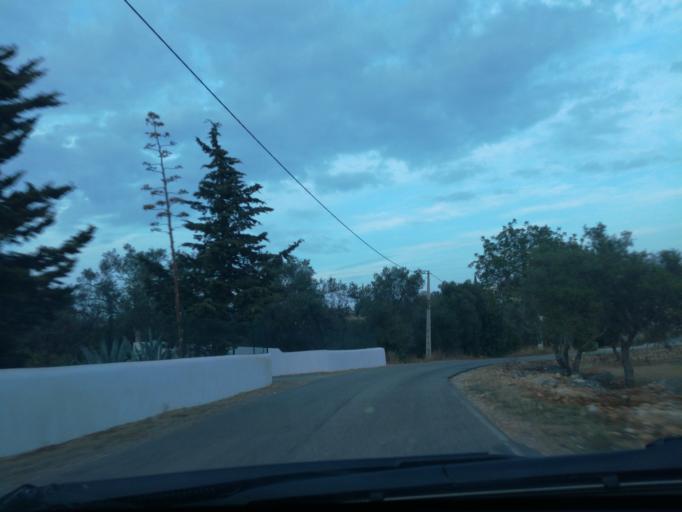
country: PT
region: Faro
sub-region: Olhao
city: Moncarapacho
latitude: 37.0831
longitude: -7.7976
